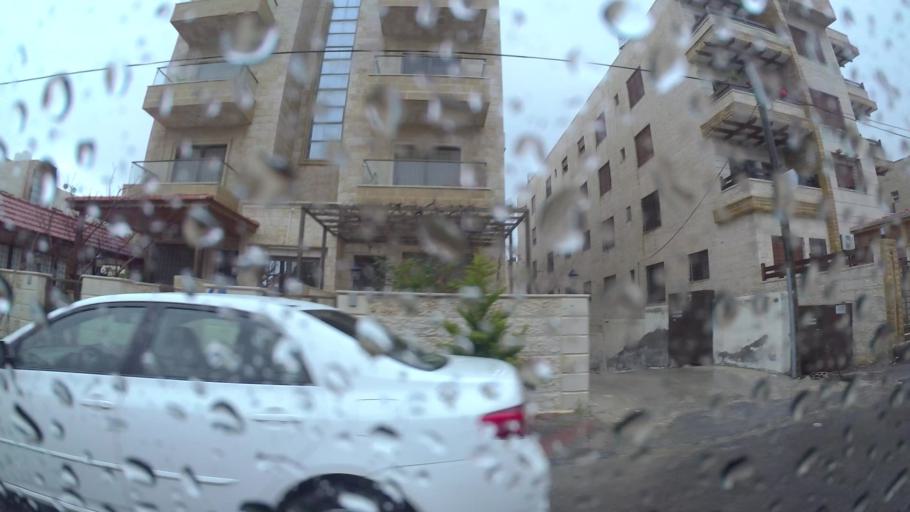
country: JO
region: Amman
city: Al Jubayhah
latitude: 32.0364
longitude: 35.8825
